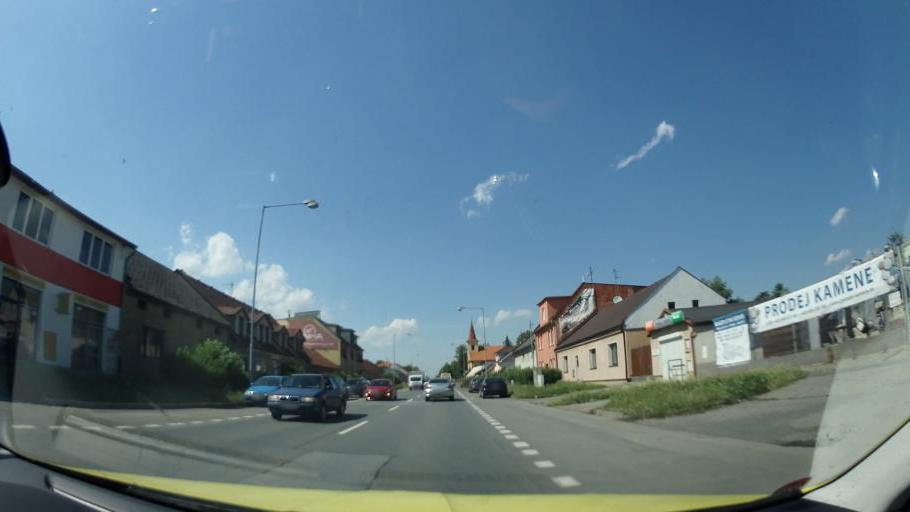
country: CZ
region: Olomoucky
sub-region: Okres Olomouc
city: Olomouc
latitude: 49.5667
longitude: 17.2618
